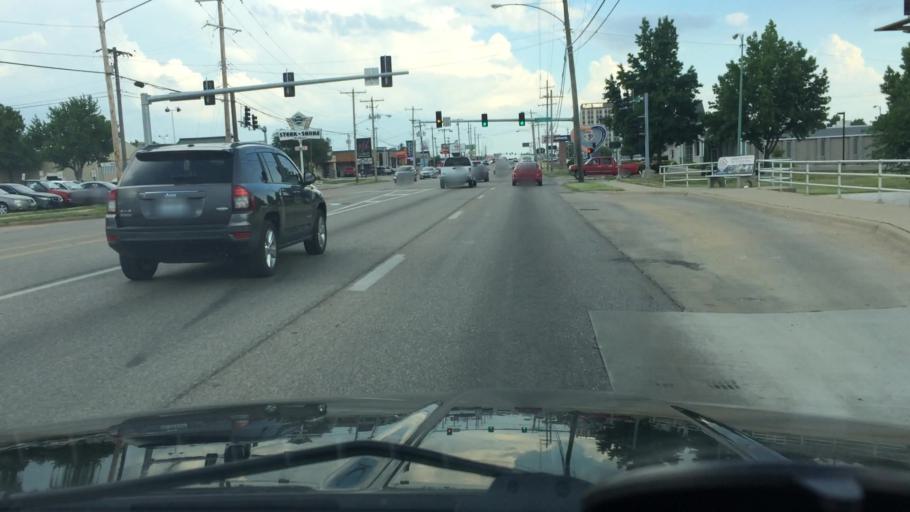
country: US
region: Missouri
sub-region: Greene County
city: Springfield
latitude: 37.1865
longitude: -93.2624
